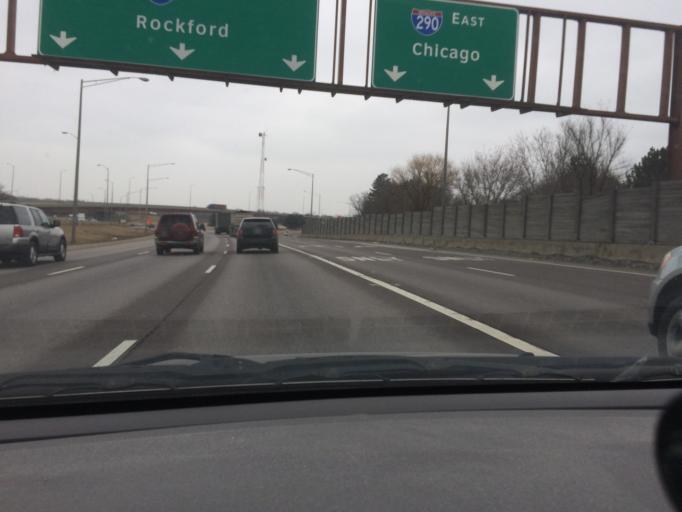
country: US
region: Illinois
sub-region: DuPage County
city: Itasca
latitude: 41.9555
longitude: -88.0288
